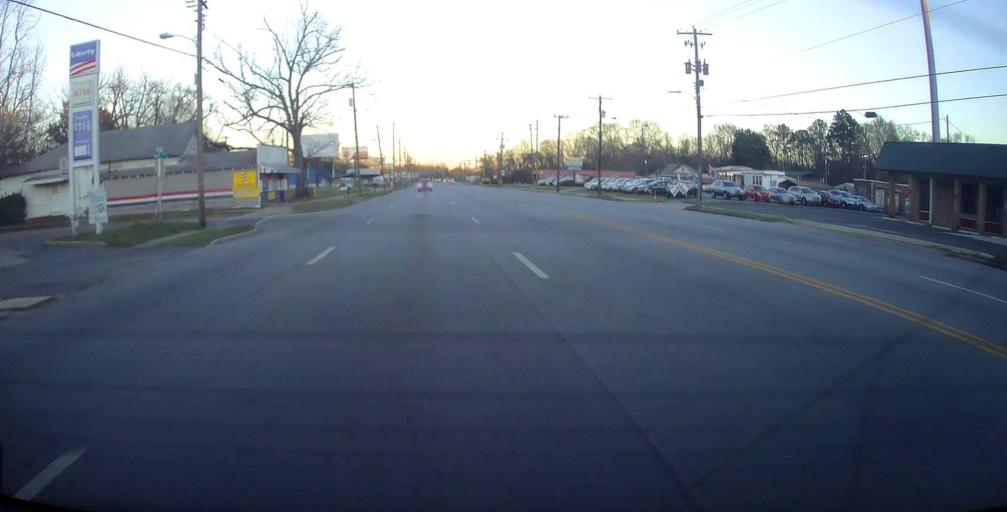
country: US
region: Alabama
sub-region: Russell County
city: Phenix City
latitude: 32.4730
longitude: -85.0136
